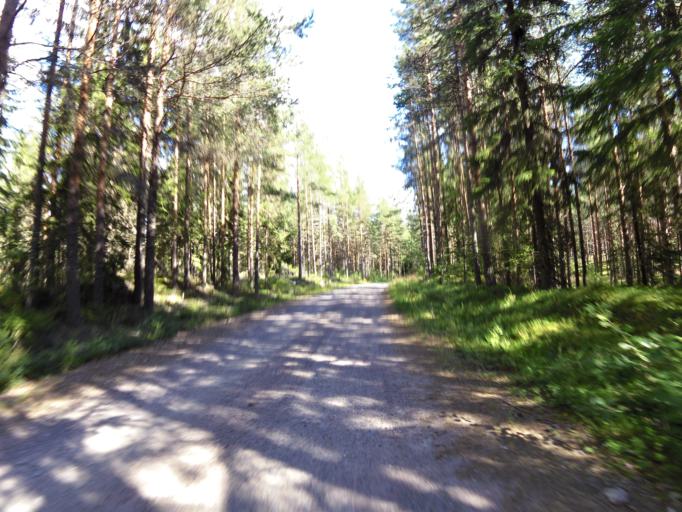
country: SE
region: Dalarna
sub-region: Faluns Kommun
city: Svardsjo
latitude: 60.6596
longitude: 15.8688
